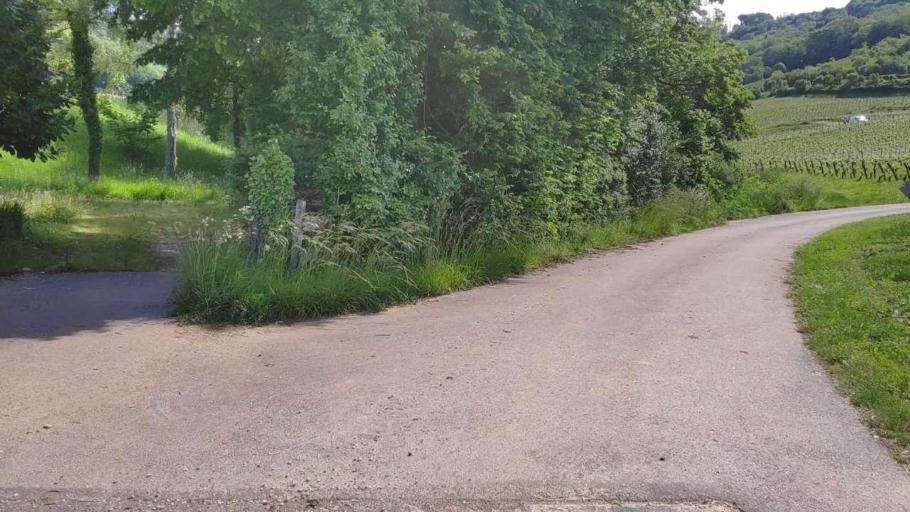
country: FR
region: Franche-Comte
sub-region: Departement du Jura
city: Perrigny
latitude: 46.7617
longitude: 5.6287
